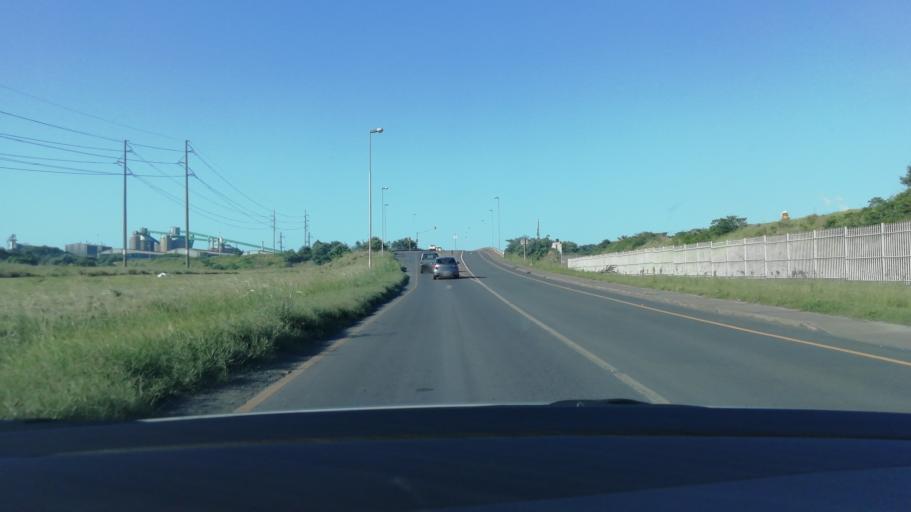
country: ZA
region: KwaZulu-Natal
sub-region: uThungulu District Municipality
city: Richards Bay
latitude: -28.7730
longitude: 32.0329
